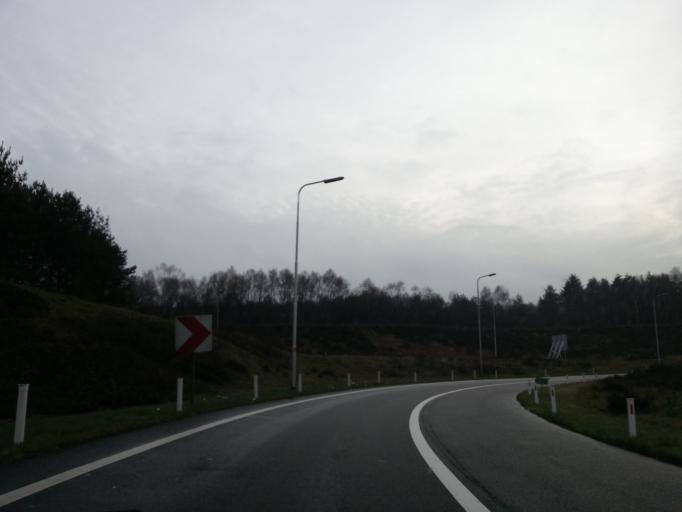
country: NL
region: Gelderland
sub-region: Gemeente Arnhem
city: Arnhem
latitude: 52.0153
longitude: 5.9231
